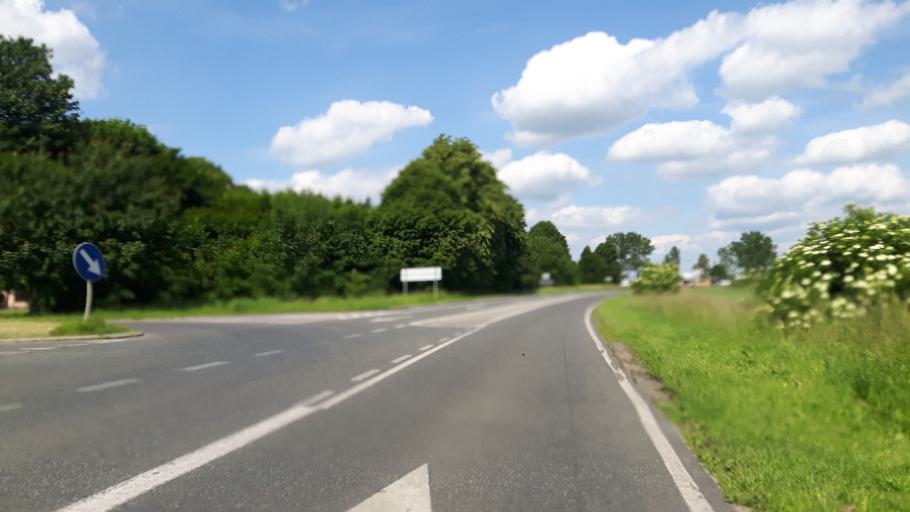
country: PL
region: West Pomeranian Voivodeship
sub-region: Powiat goleniowski
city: Nowogard
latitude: 53.6816
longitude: 15.1192
